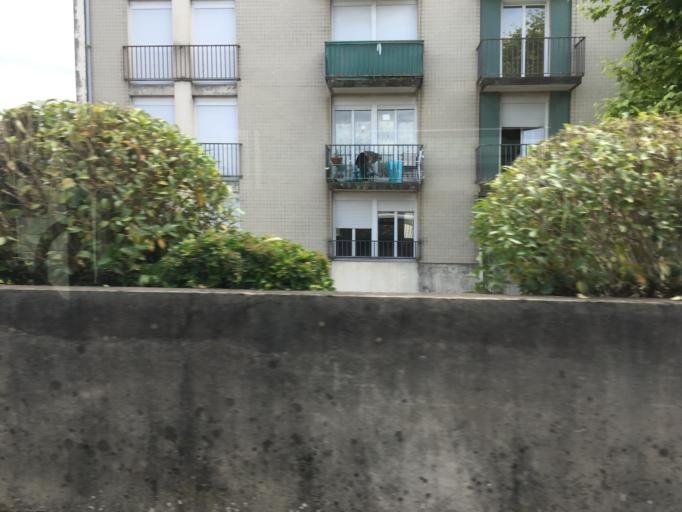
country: FR
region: Aquitaine
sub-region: Departement de la Gironde
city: Begles
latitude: 44.8198
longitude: -0.5621
